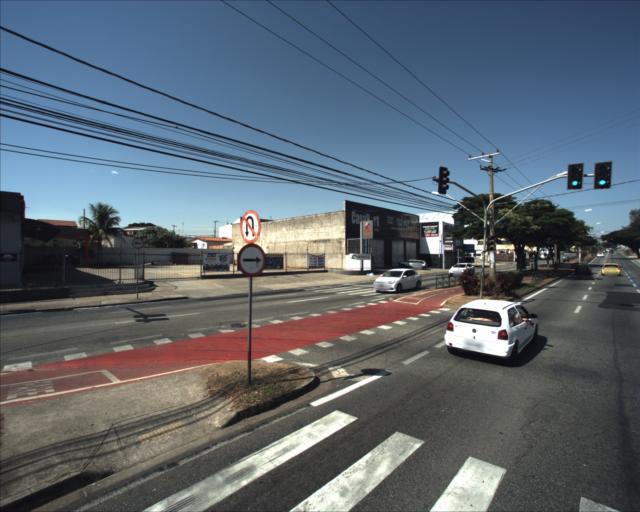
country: BR
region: Sao Paulo
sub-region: Sorocaba
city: Sorocaba
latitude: -23.4740
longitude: -47.4763
